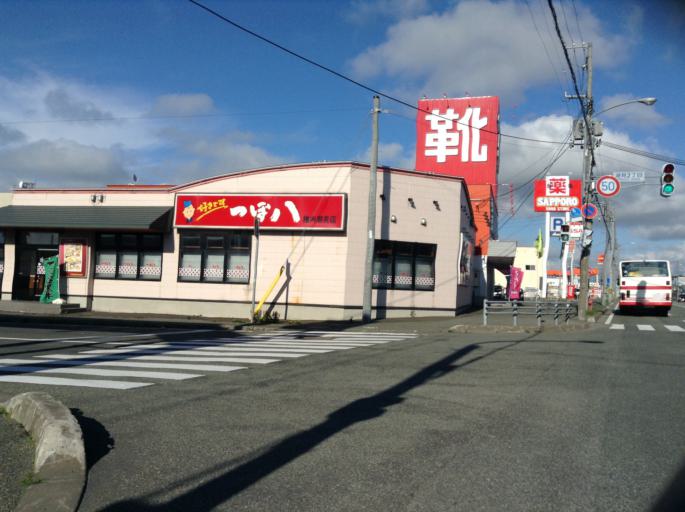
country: JP
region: Hokkaido
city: Wakkanai
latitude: 45.3961
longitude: 141.6987
